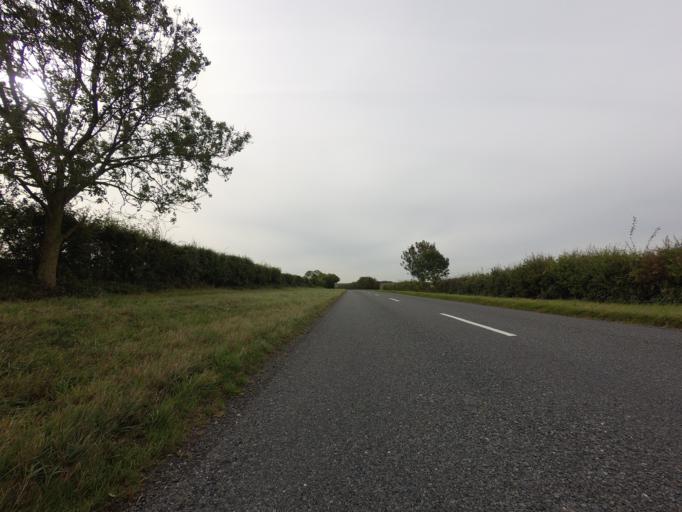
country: GB
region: England
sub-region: Cambridgeshire
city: Melbourn
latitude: 52.0475
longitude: 0.0456
